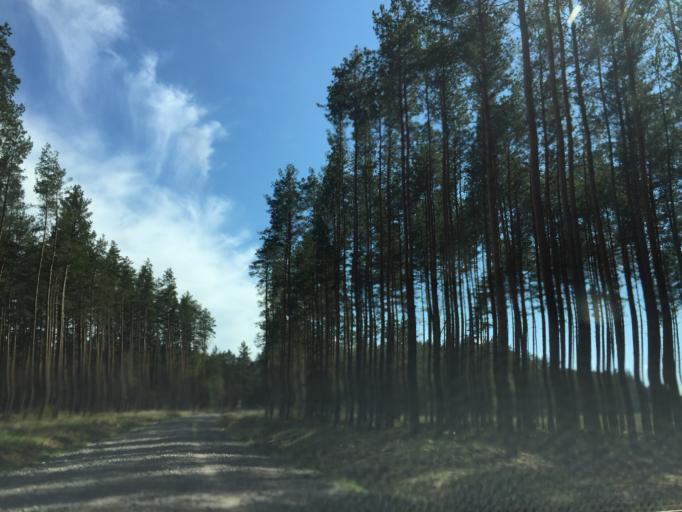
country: LV
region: Strenci
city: Strenci
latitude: 57.5810
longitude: 25.7116
